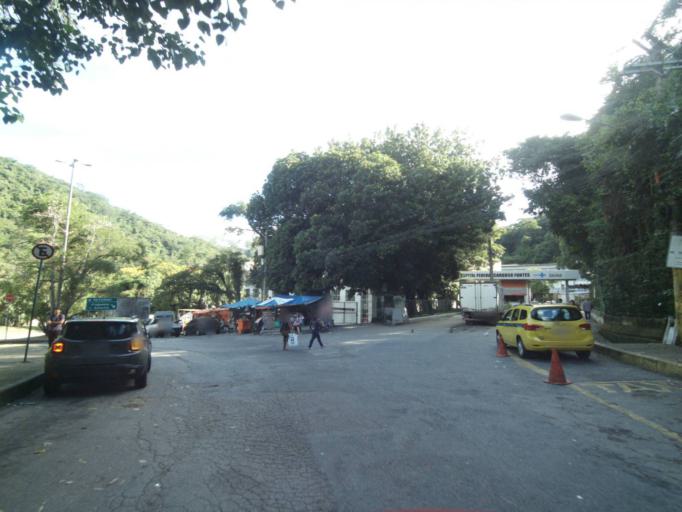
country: BR
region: Rio de Janeiro
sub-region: Rio De Janeiro
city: Rio de Janeiro
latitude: -22.9248
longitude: -43.3150
